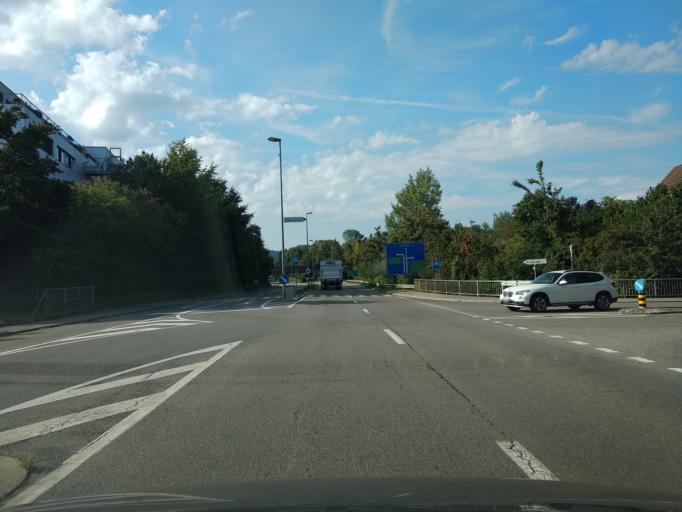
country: CH
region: Thurgau
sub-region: Frauenfeld District
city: Frauenfeld
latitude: 47.5631
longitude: 8.8706
